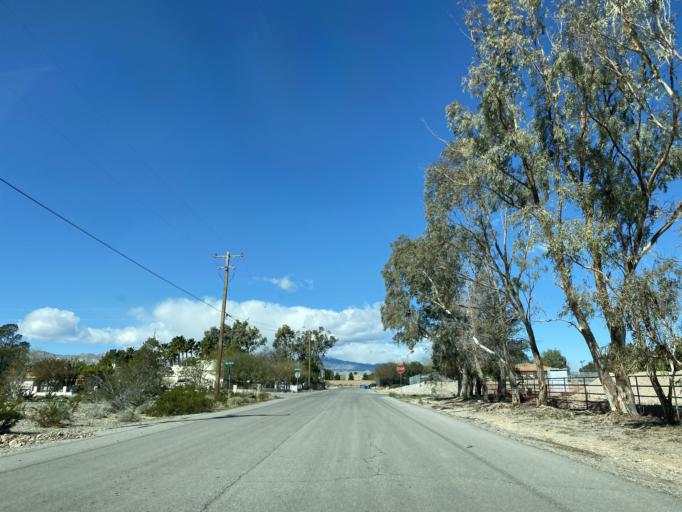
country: US
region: Nevada
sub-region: Clark County
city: North Las Vegas
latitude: 36.3267
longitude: -115.2845
